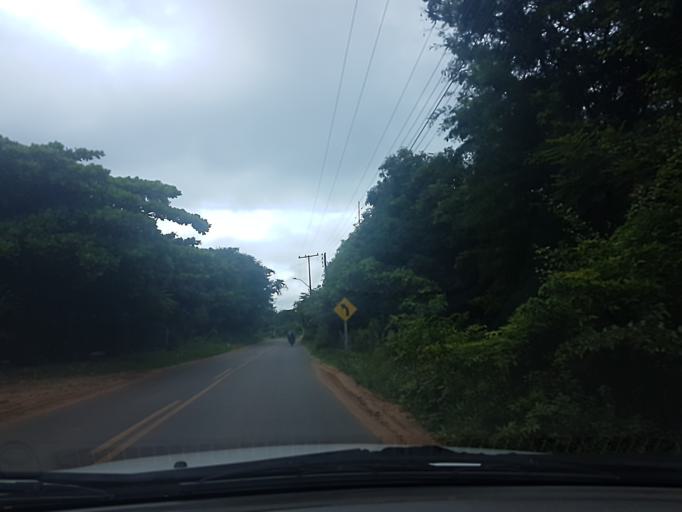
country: PY
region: Central
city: Limpio
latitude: -25.1947
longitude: -57.4600
